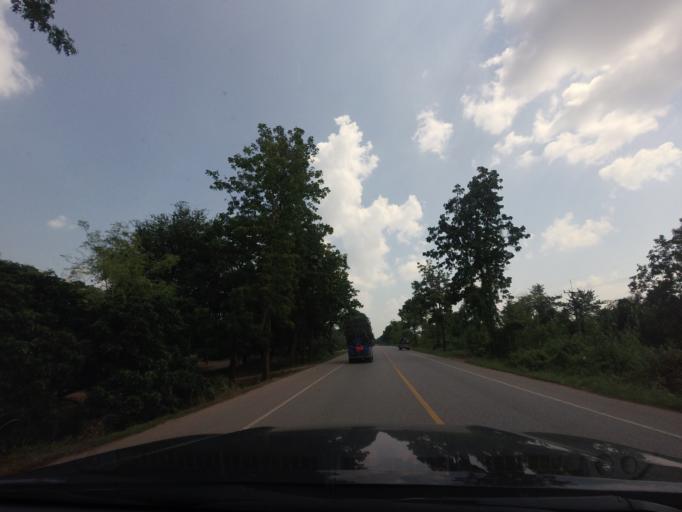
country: TH
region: Phitsanulok
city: Chat Trakan
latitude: 17.2785
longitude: 100.5387
